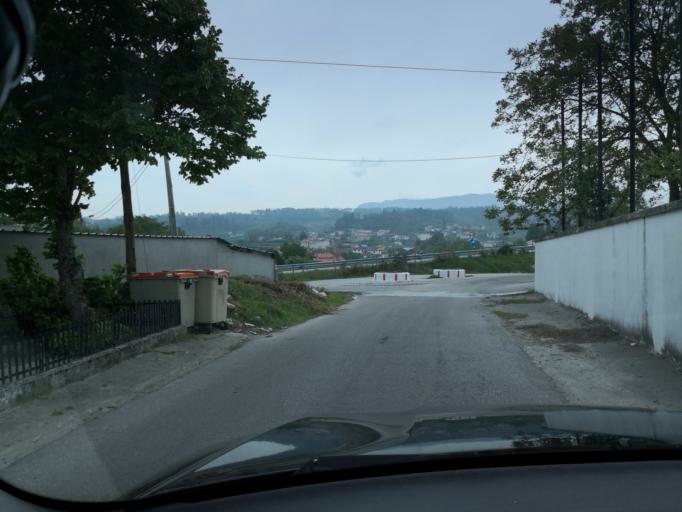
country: PT
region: Vila Real
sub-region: Vila Real
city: Vila Real
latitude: 41.2858
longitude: -7.8082
